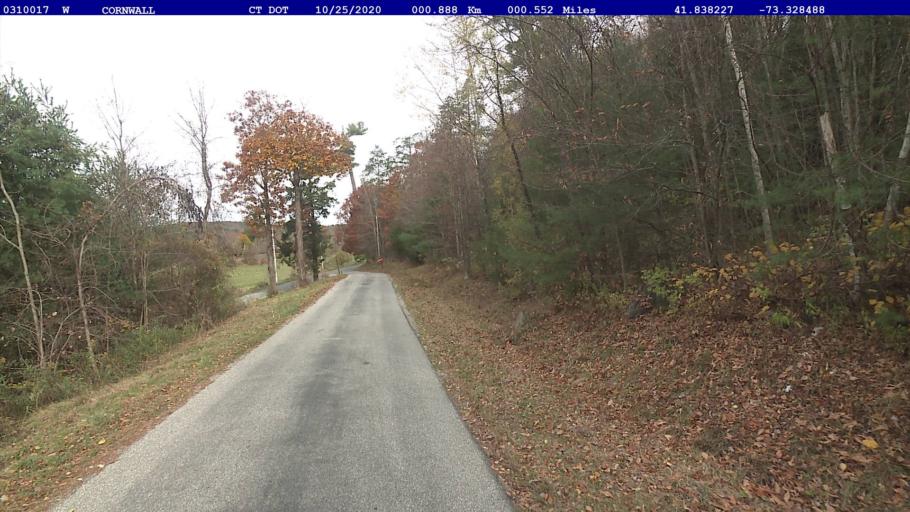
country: US
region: Connecticut
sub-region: Litchfield County
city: New Preston
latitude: 41.8382
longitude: -73.3285
